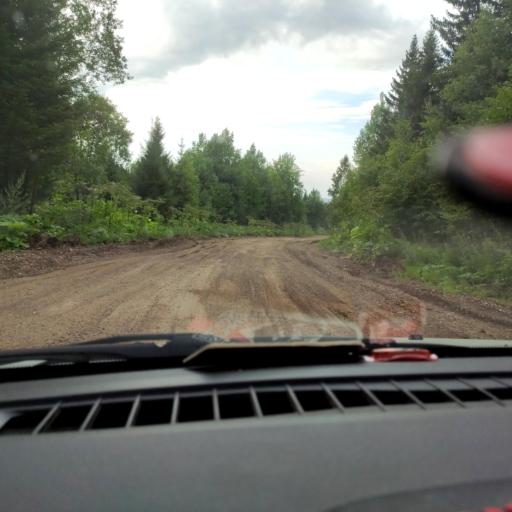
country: RU
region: Perm
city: Kultayevo
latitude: 57.8142
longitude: 56.0014
